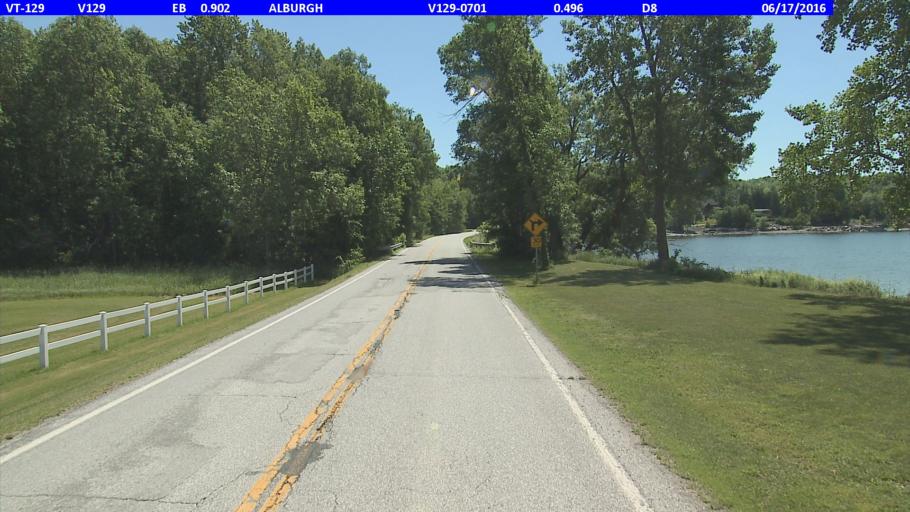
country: US
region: Vermont
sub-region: Grand Isle County
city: North Hero
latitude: 44.9036
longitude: -73.3063
